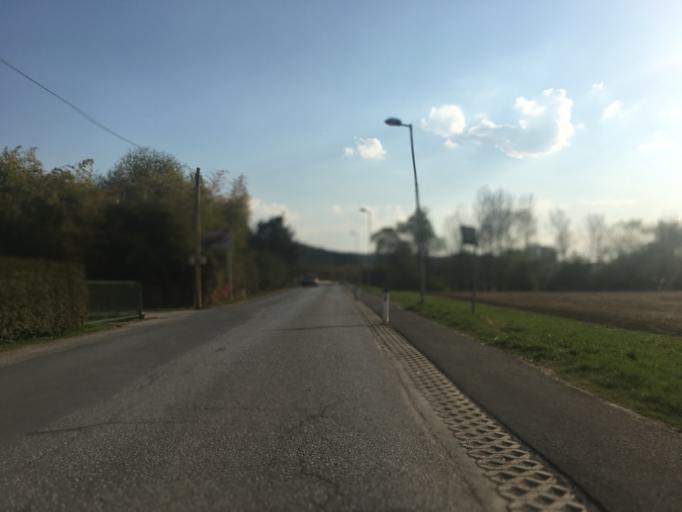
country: AT
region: Styria
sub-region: Politischer Bezirk Weiz
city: Ungerdorf
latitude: 47.0994
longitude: 15.6844
